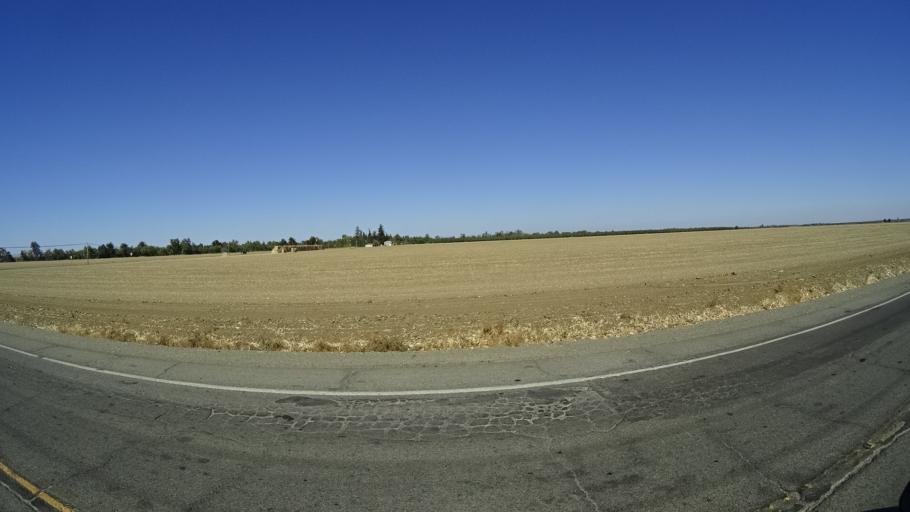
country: US
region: California
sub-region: Yolo County
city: Davis
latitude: 38.5611
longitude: -121.8387
